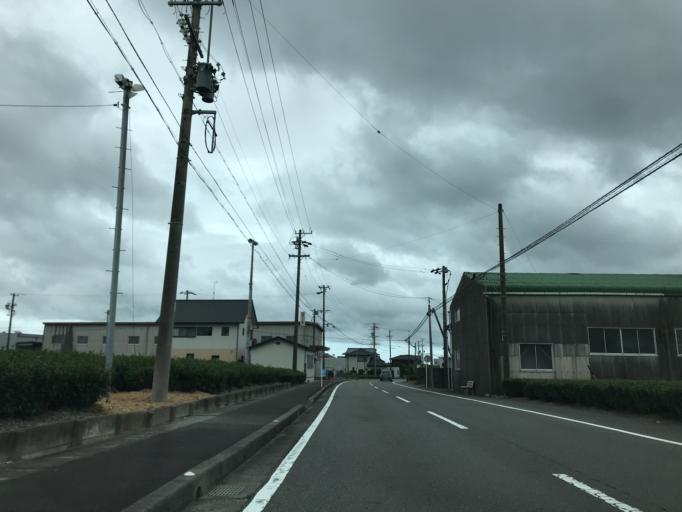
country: JP
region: Shizuoka
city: Kanaya
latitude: 34.7484
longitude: 138.1355
